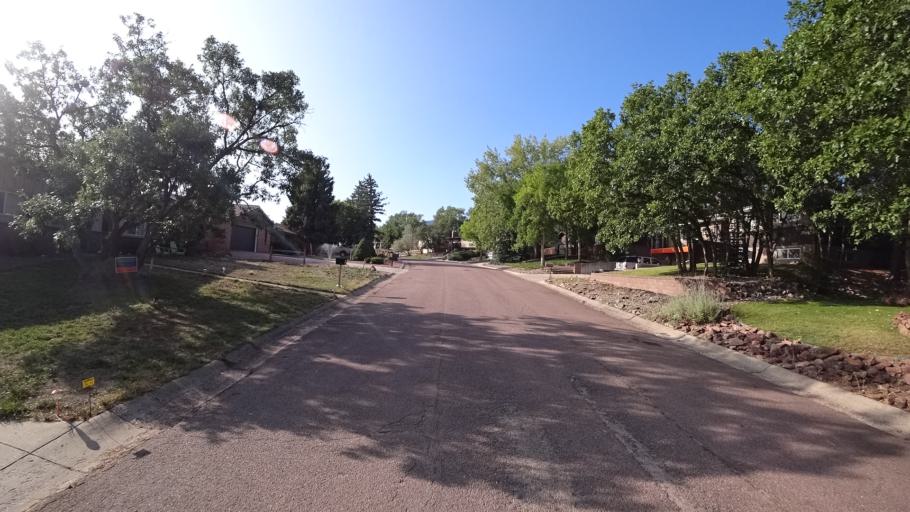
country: US
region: Colorado
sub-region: El Paso County
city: Colorado Springs
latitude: 38.8207
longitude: -104.8666
